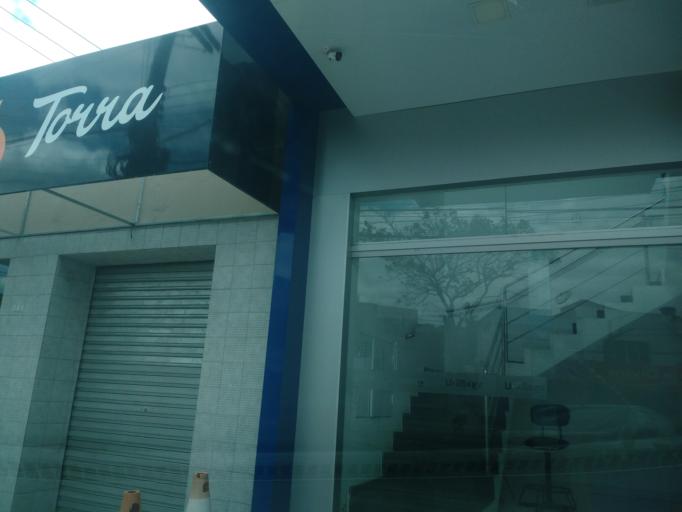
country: BR
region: Alagoas
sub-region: Uniao Dos Palmares
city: Uniao dos Palmares
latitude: -9.1568
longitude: -36.0329
